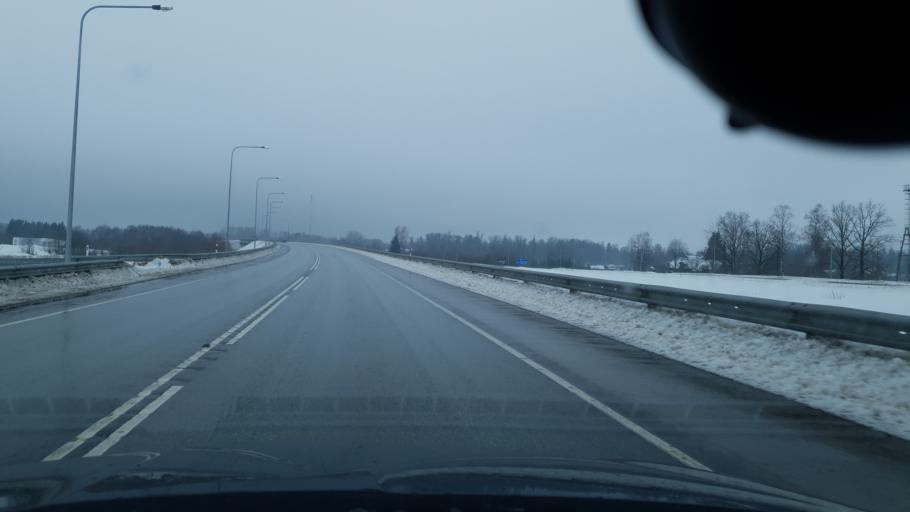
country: EE
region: Jogevamaa
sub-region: Jogeva linn
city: Jogeva
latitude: 58.5666
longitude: 26.2909
